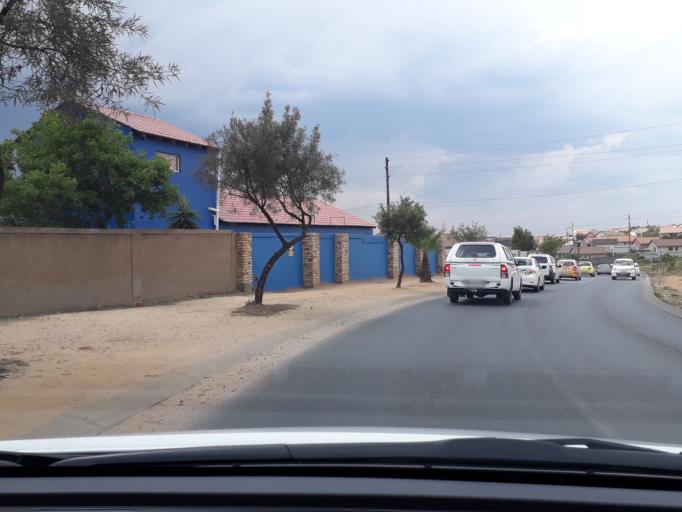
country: ZA
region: Gauteng
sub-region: West Rand District Municipality
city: Muldersdriseloop
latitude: -26.0428
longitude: 27.9222
